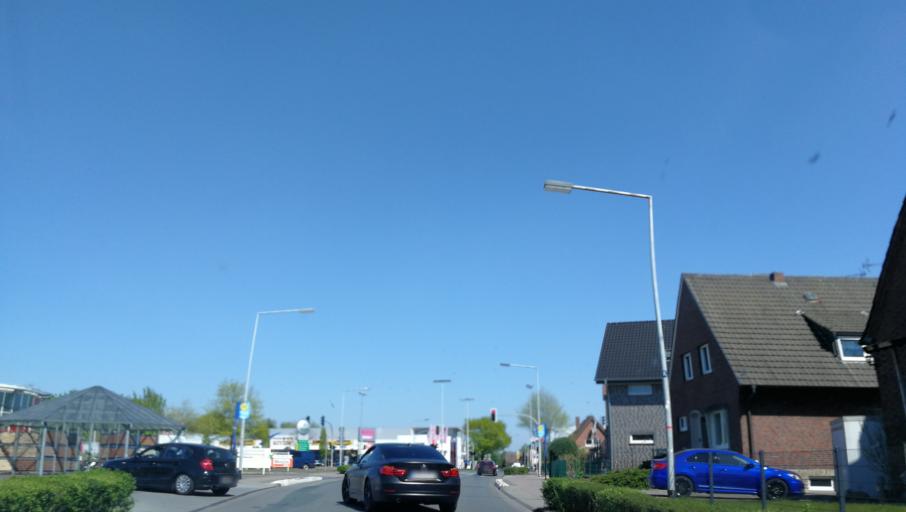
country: DE
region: North Rhine-Westphalia
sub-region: Regierungsbezirk Munster
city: Rheine
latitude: 52.2661
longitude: 7.4457
